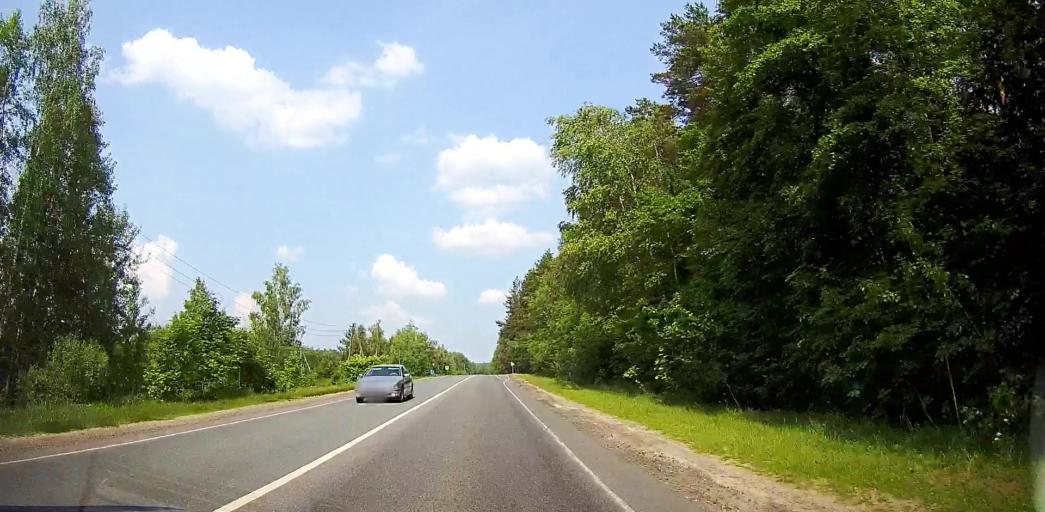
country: RU
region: Moskovskaya
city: Stupino
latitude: 54.9747
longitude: 38.1550
